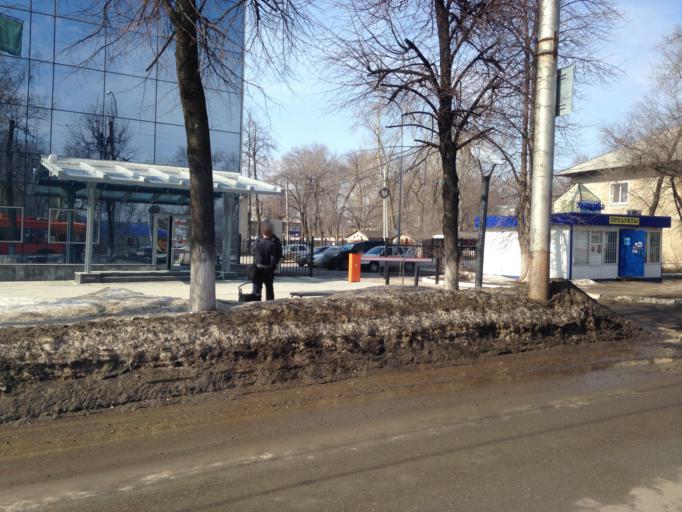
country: RU
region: Ulyanovsk
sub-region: Ulyanovskiy Rayon
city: Ulyanovsk
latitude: 54.3470
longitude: 48.5486
